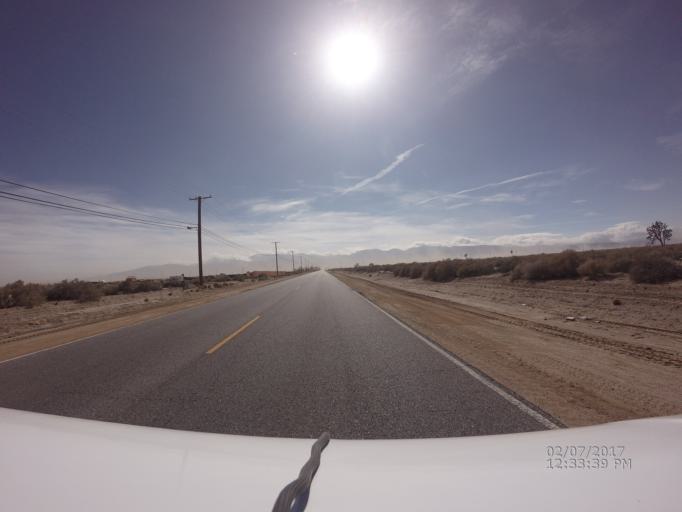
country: US
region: California
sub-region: Los Angeles County
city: Lake Los Angeles
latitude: 34.5852
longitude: -117.8267
